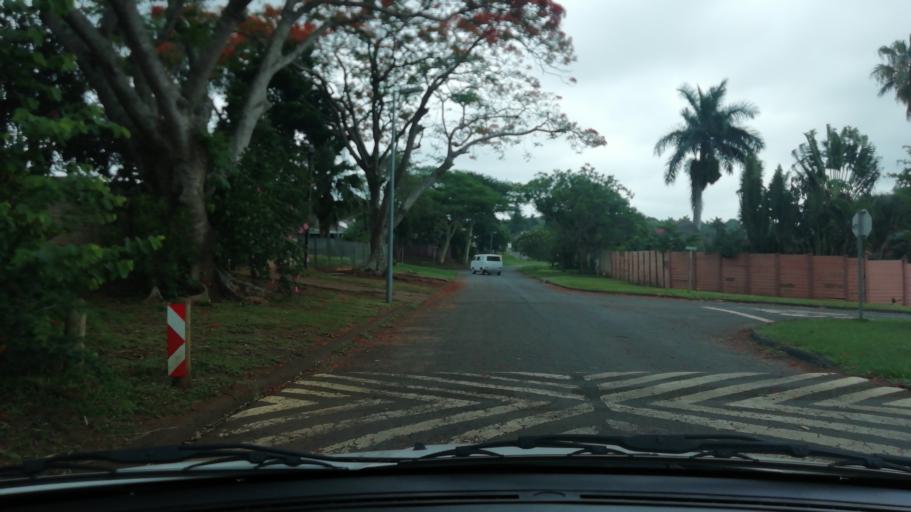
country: ZA
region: KwaZulu-Natal
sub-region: uThungulu District Municipality
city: Empangeni
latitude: -28.7650
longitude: 31.8997
